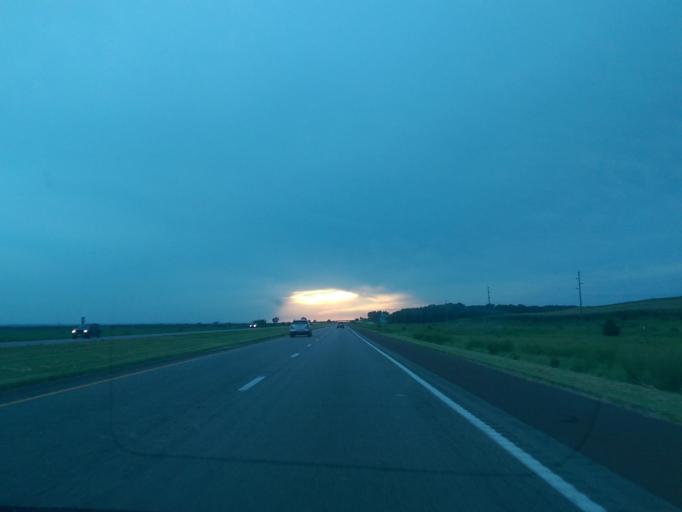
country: US
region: Missouri
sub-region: Holt County
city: Mound City
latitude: 40.1532
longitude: -95.2554
